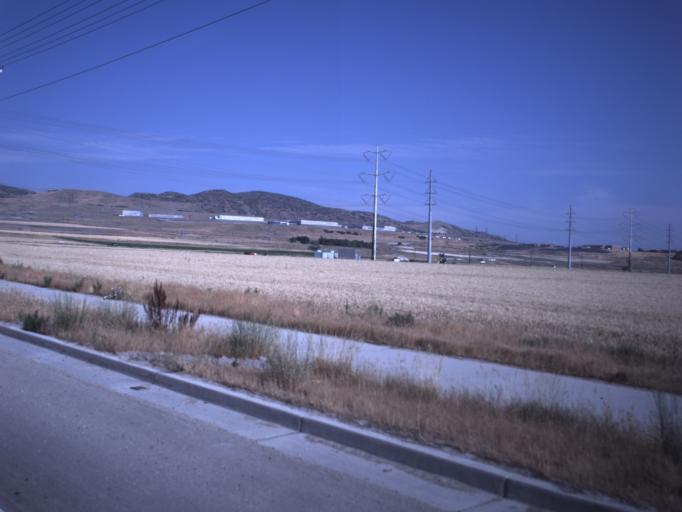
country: US
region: Utah
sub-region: Utah County
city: Lehi
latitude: 40.4132
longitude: -111.9074
